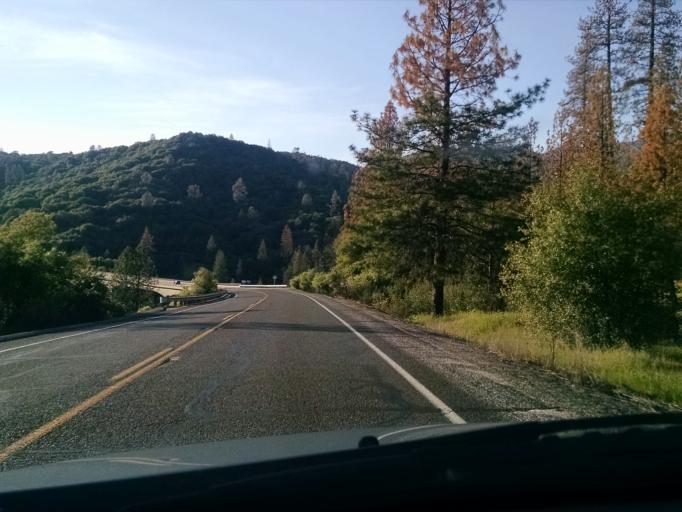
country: US
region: California
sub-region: Madera County
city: Ahwahnee
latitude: 37.4443
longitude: -119.7439
